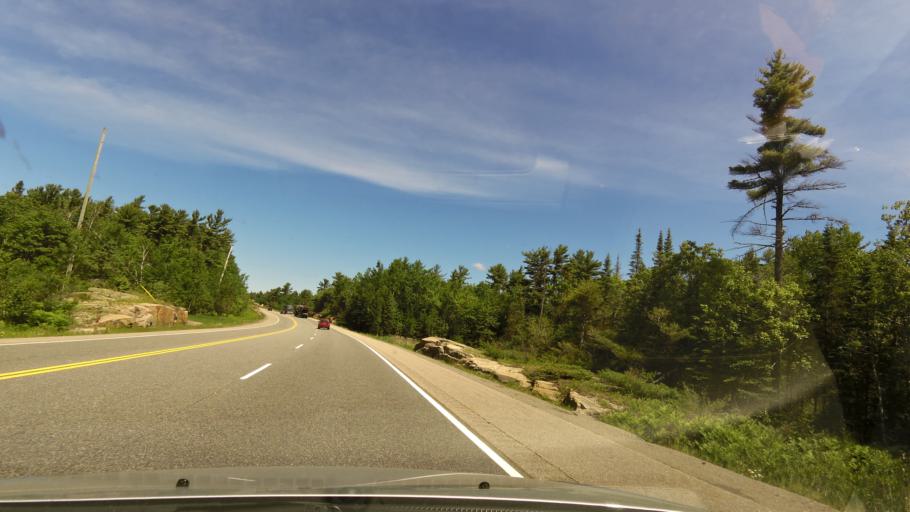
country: CA
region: Ontario
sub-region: Parry Sound District
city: Parry Sound
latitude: 45.6166
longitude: -80.3834
